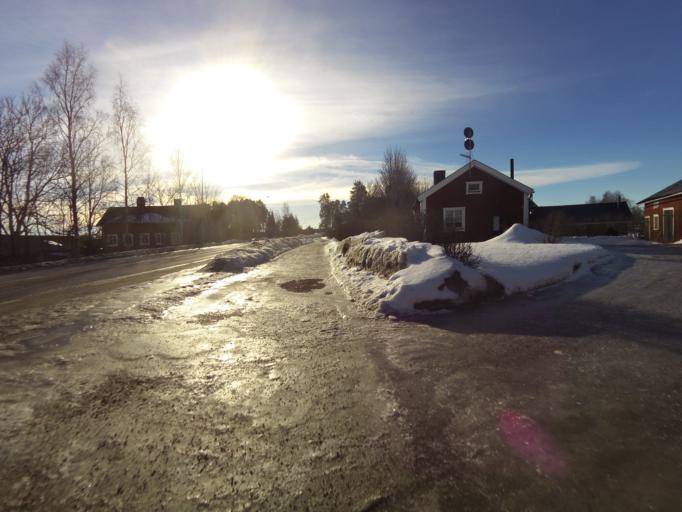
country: SE
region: Gaevleborg
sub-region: Gavle Kommun
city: Valbo
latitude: 60.6222
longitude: 16.9796
